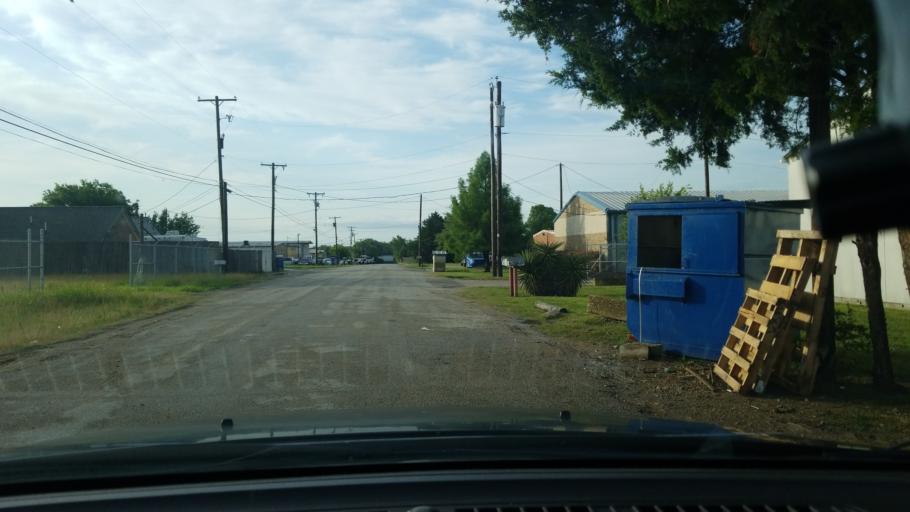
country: US
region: Texas
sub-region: Dallas County
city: Mesquite
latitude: 32.7969
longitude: -96.6220
